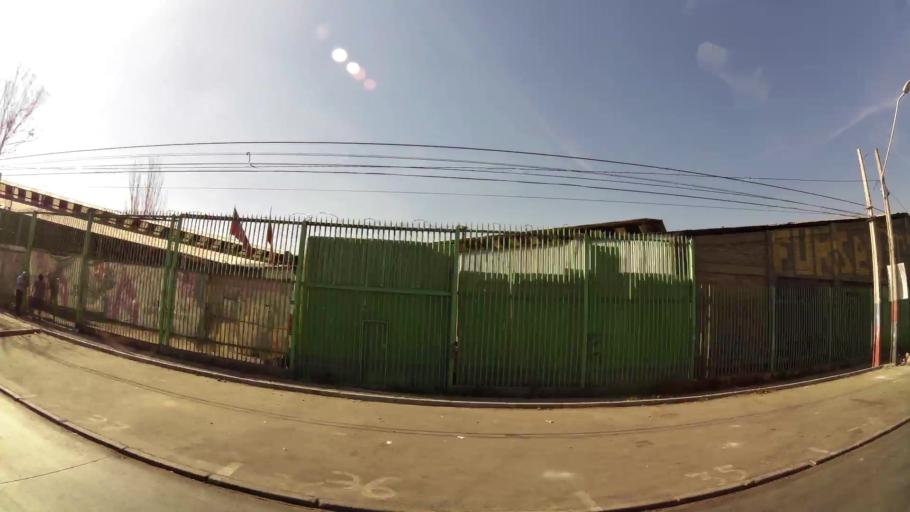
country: CL
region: Santiago Metropolitan
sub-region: Provincia de Santiago
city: Villa Presidente Frei, Nunoa, Santiago, Chile
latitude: -33.4766
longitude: -70.5712
